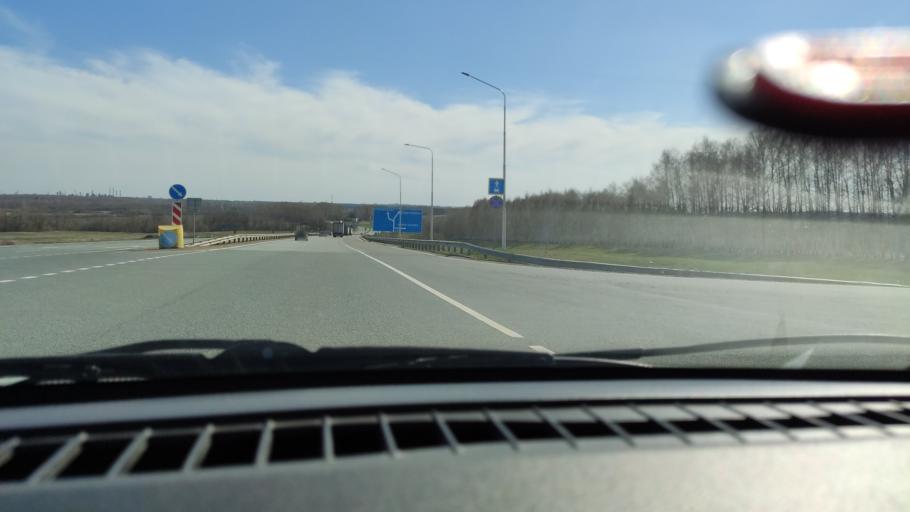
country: RU
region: Bashkortostan
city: Sterlitamak
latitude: 53.7516
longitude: 55.9440
